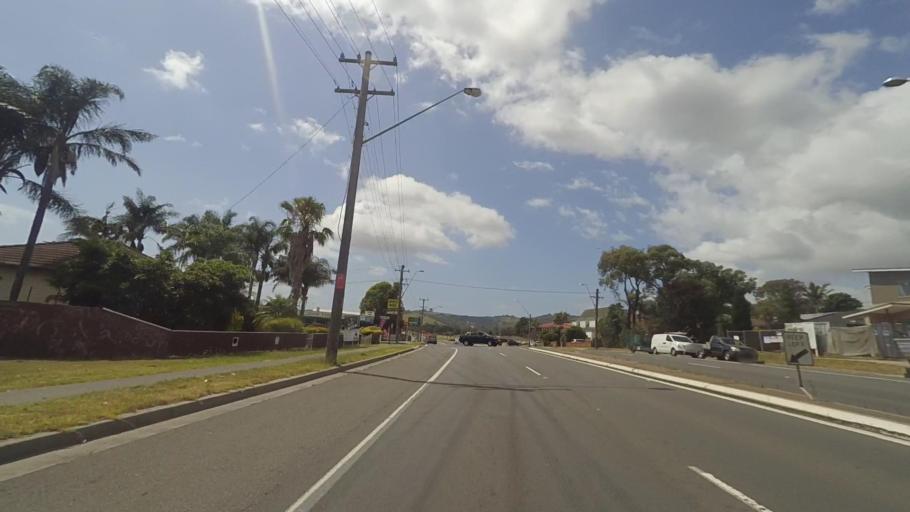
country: AU
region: New South Wales
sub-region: Shellharbour
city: Albion Park Rail
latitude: -34.5660
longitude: 150.8005
